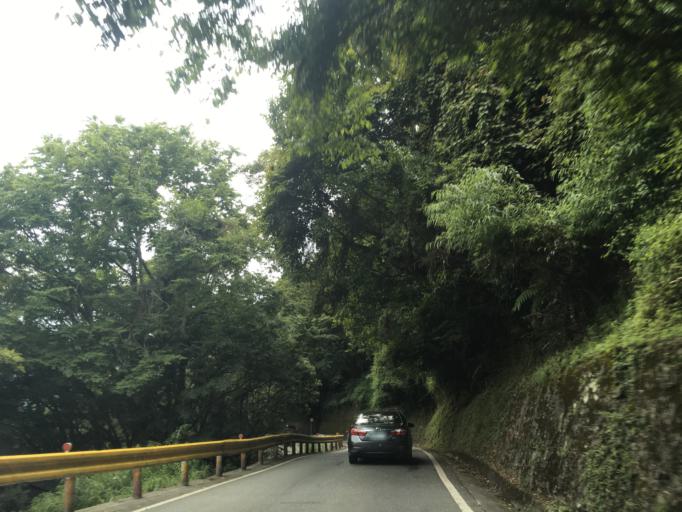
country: TW
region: Taiwan
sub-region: Hualien
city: Hualian
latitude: 24.1753
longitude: 121.3817
